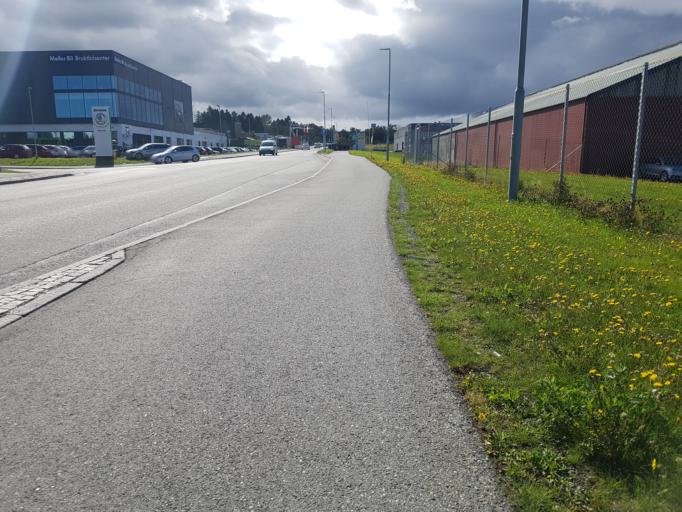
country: NO
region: Sor-Trondelag
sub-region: Trondheim
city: Trondheim
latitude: 63.4234
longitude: 10.4645
